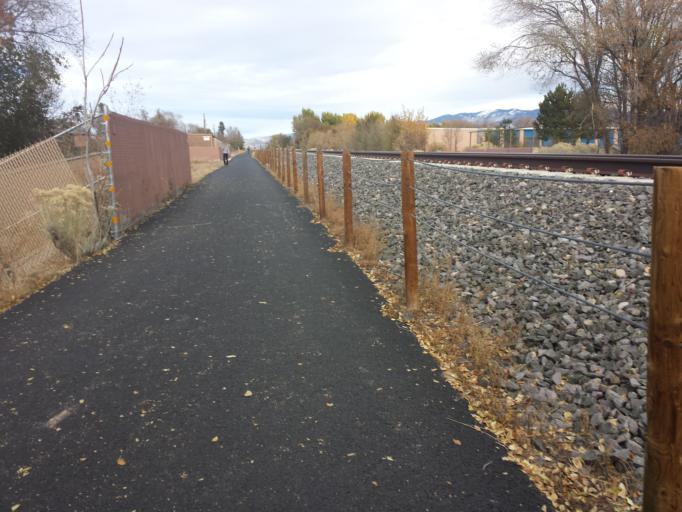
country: US
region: New Mexico
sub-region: Santa Fe County
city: Santa Fe
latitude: 35.6646
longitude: -105.9631
